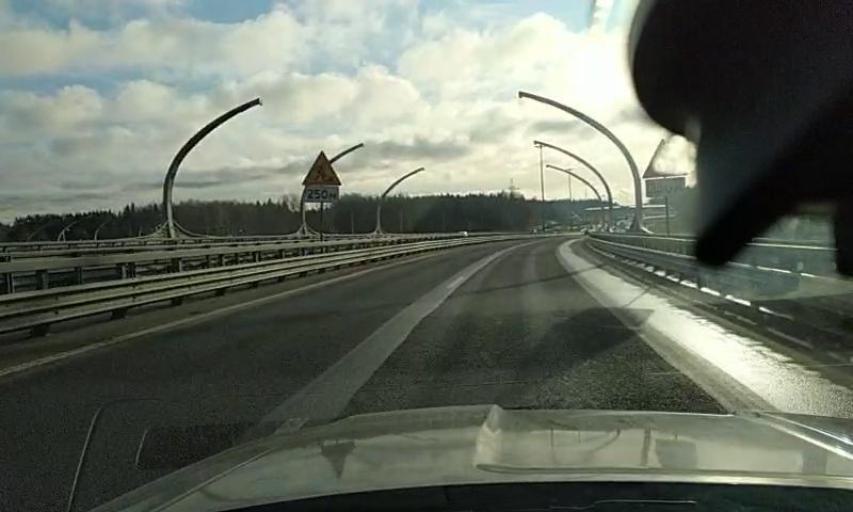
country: RU
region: St.-Petersburg
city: Beloostrov
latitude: 60.1352
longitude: 30.0585
